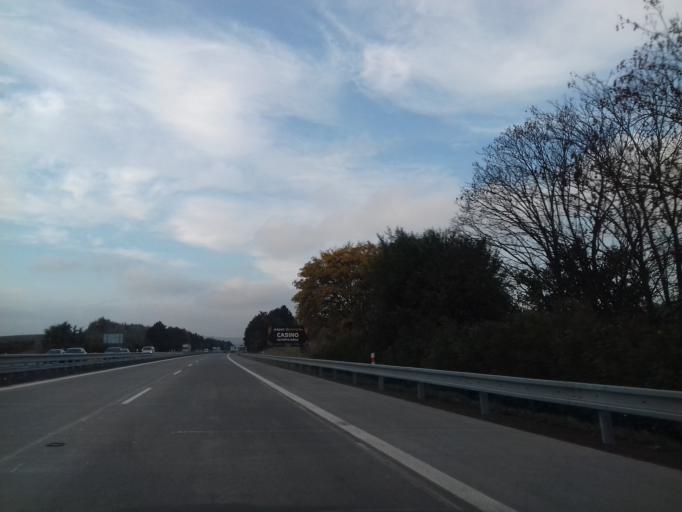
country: CZ
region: South Moravian
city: Velke Nemcice
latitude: 48.9798
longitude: 16.6975
